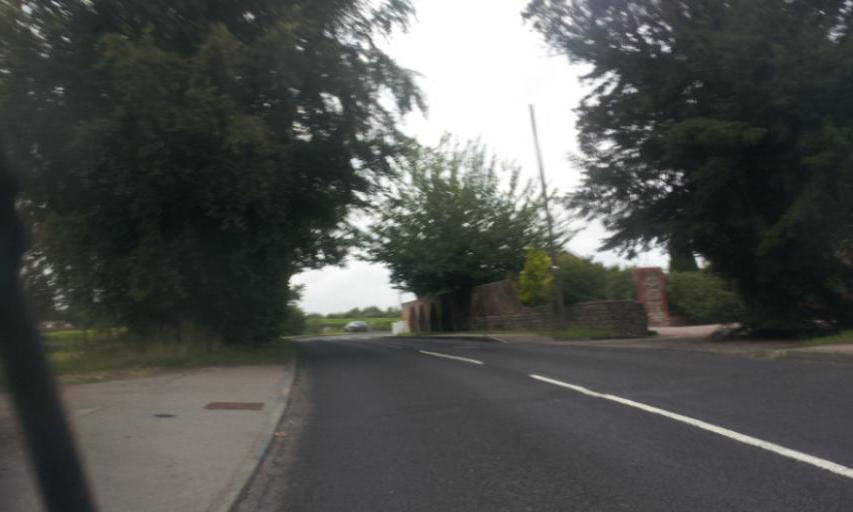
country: GB
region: England
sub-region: Kent
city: Wateringbury
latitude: 51.2614
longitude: 0.4314
